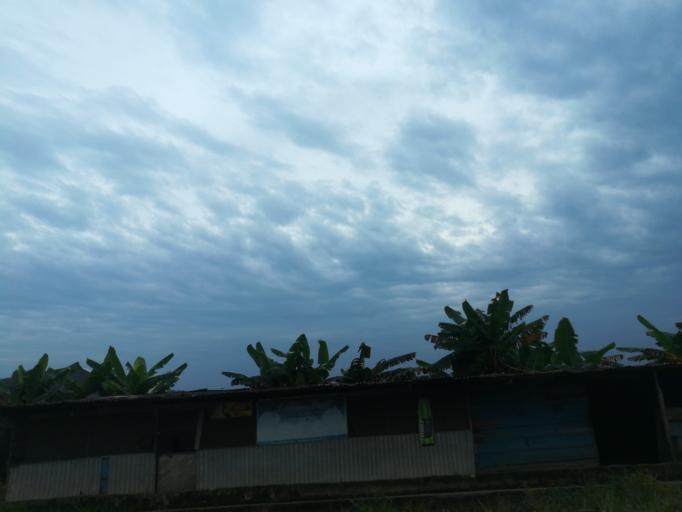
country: NG
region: Rivers
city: Port Harcourt
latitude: 4.7962
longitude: 6.9547
